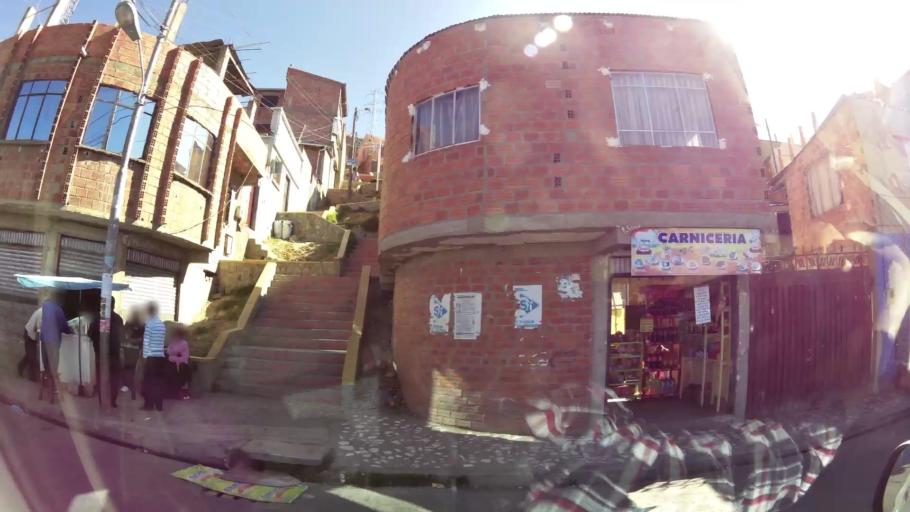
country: BO
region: La Paz
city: La Paz
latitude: -16.5128
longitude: -68.1483
